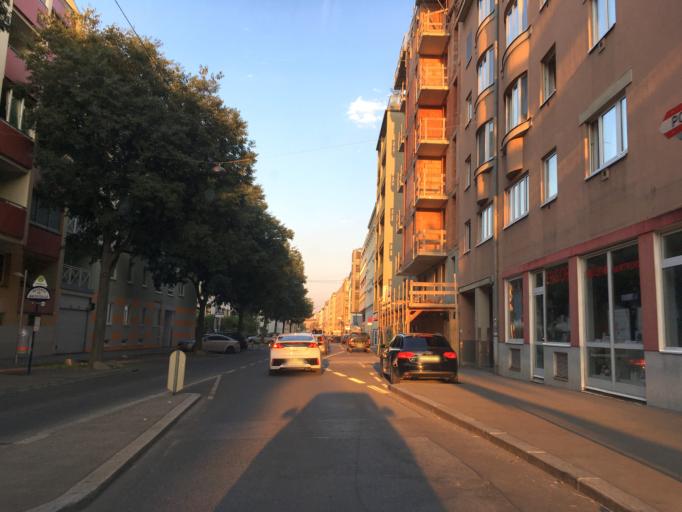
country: AT
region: Vienna
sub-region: Wien Stadt
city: Vienna
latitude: 48.1705
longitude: 16.3617
